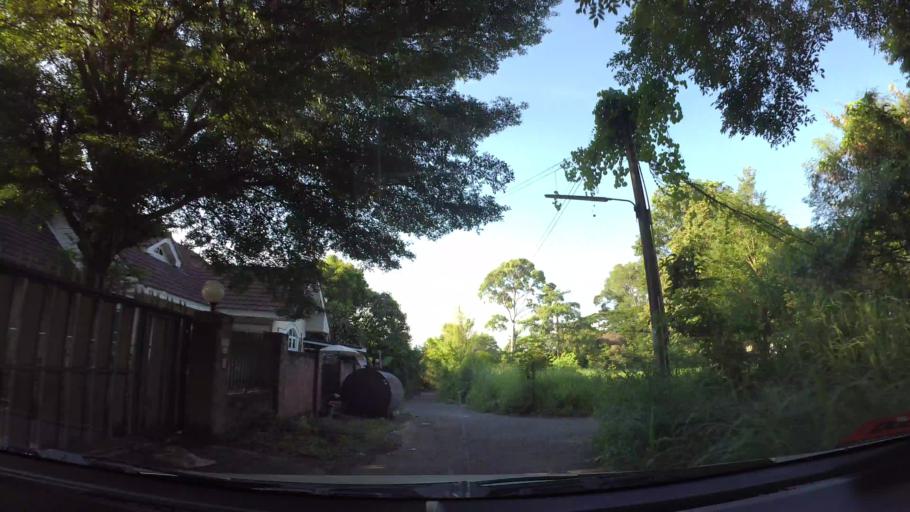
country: TH
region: Chon Buri
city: Si Racha
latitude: 13.1438
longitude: 100.9346
